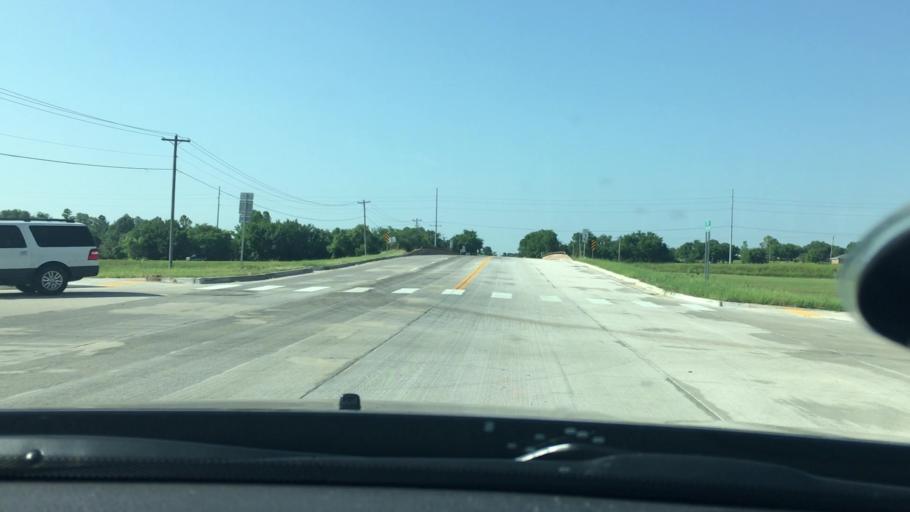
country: US
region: Oklahoma
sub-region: Pontotoc County
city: Ada
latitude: 34.7535
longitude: -96.6701
